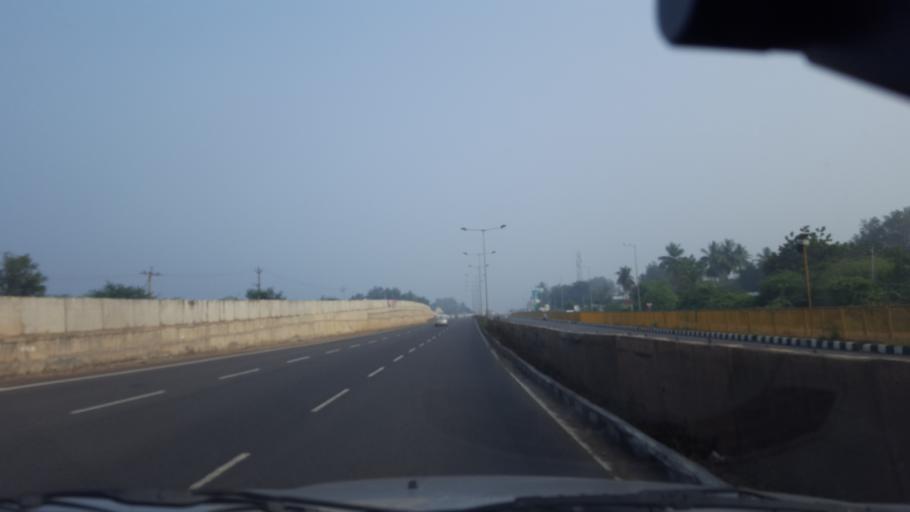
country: IN
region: Andhra Pradesh
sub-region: Prakasam
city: Ongole
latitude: 15.4199
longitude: 80.0393
